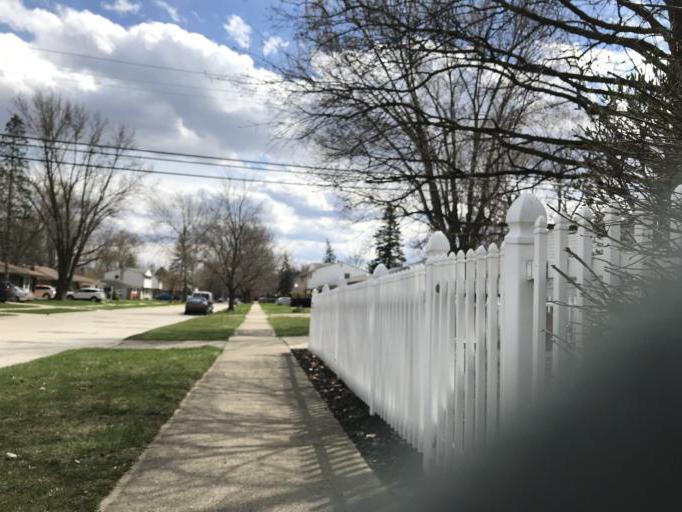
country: US
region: Michigan
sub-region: Oakland County
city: Farmington
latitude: 42.4629
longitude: -83.3461
